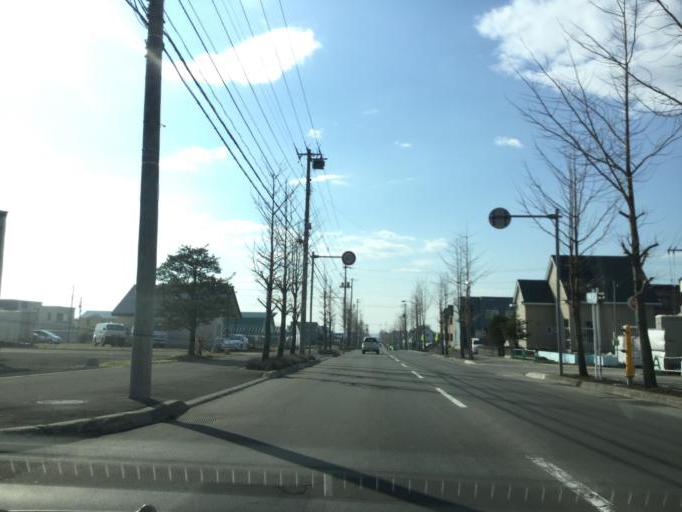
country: JP
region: Hokkaido
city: Ebetsu
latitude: 43.0855
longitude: 141.5384
